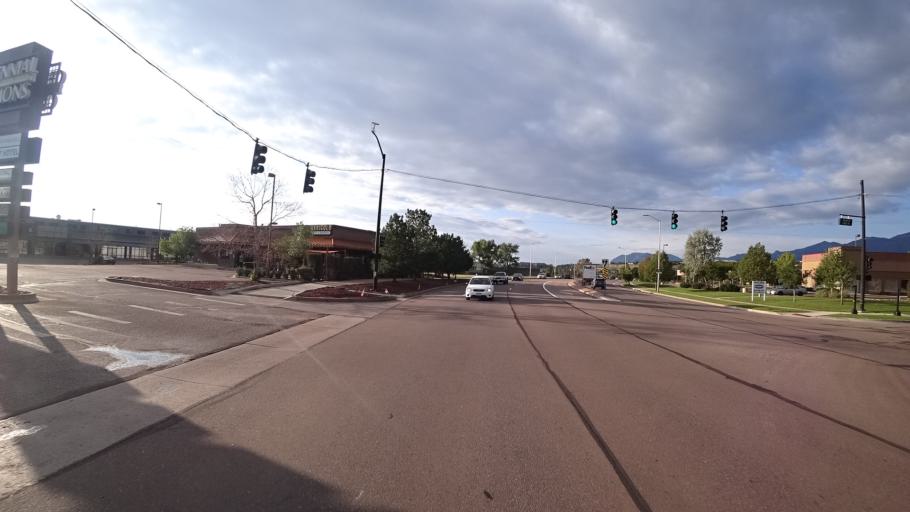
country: US
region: Colorado
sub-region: El Paso County
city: Colorado Springs
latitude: 38.8990
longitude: -104.8511
